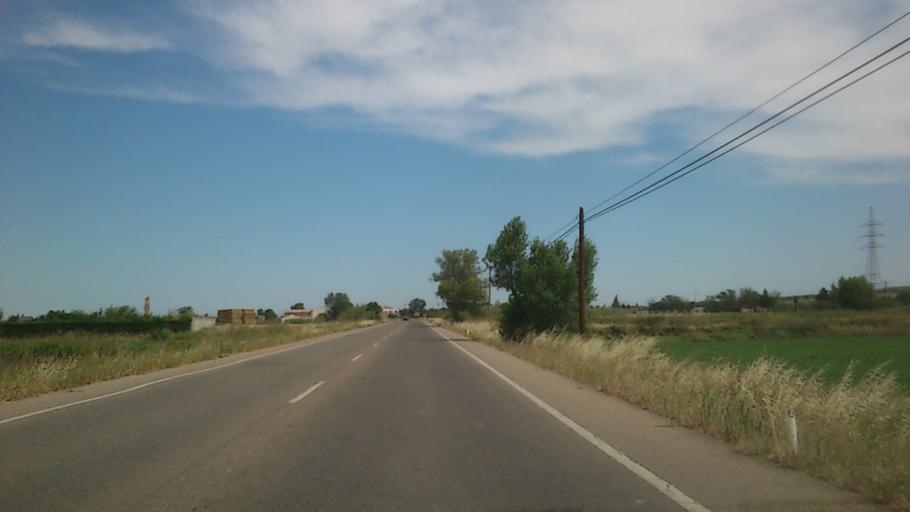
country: ES
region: Aragon
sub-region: Provincia de Zaragoza
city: Villanueva de Gallego
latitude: 41.7522
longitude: -0.8000
